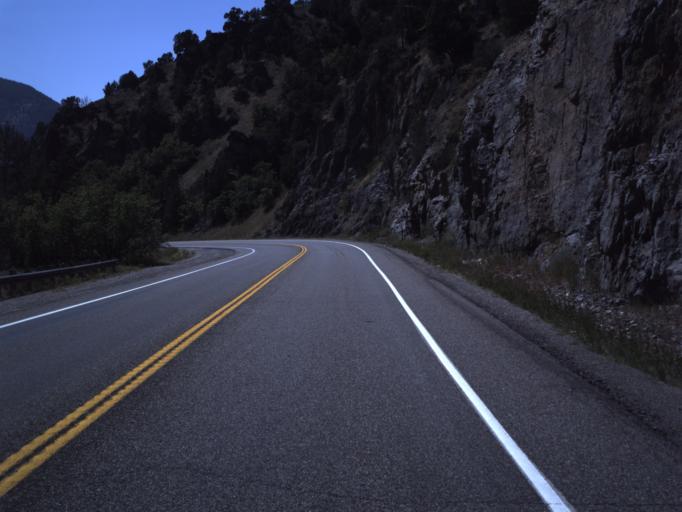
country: US
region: Utah
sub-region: Cache County
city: North Logan
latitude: 41.7763
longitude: -111.6502
